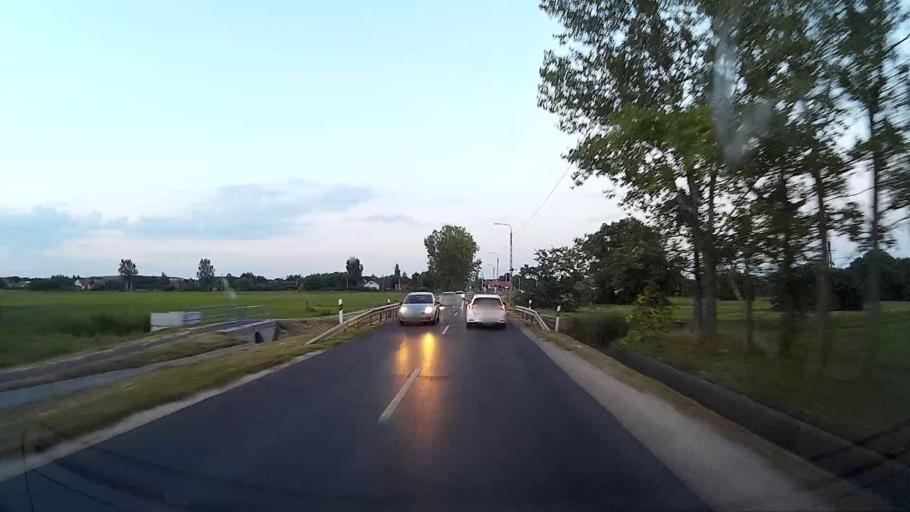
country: HU
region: Pest
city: Albertirsa
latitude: 47.2444
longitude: 19.6267
